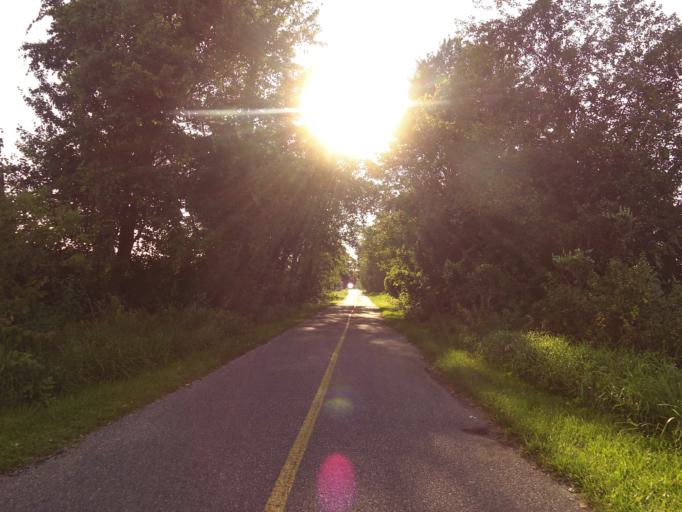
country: CA
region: Ontario
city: Bells Corners
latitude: 45.3424
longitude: -75.8446
